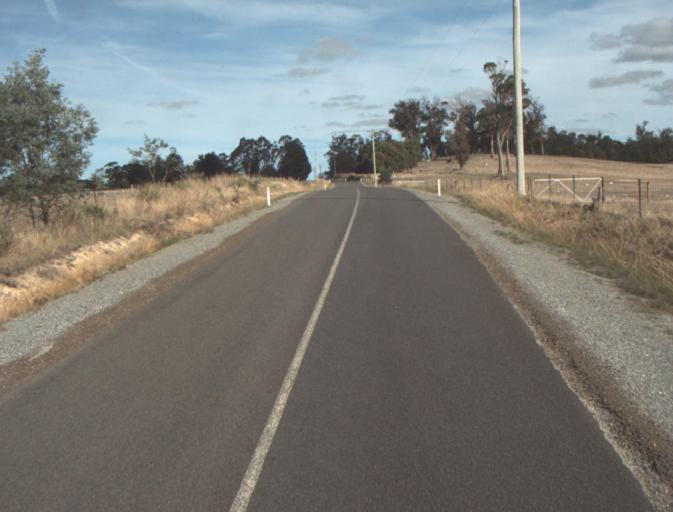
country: AU
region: Tasmania
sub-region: Launceston
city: Mayfield
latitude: -41.2118
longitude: 147.1340
